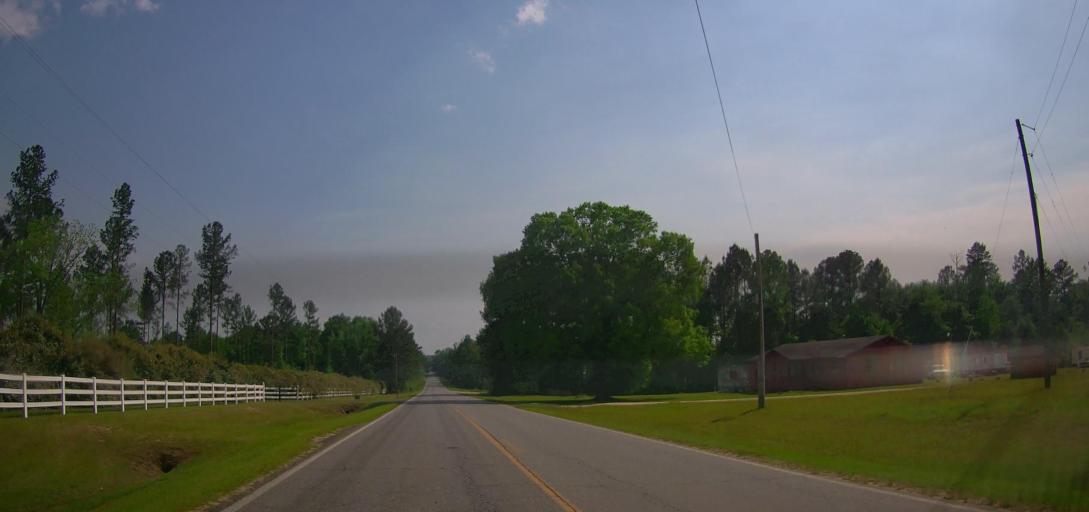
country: US
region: Georgia
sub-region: Laurens County
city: East Dublin
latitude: 32.5755
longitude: -82.8645
